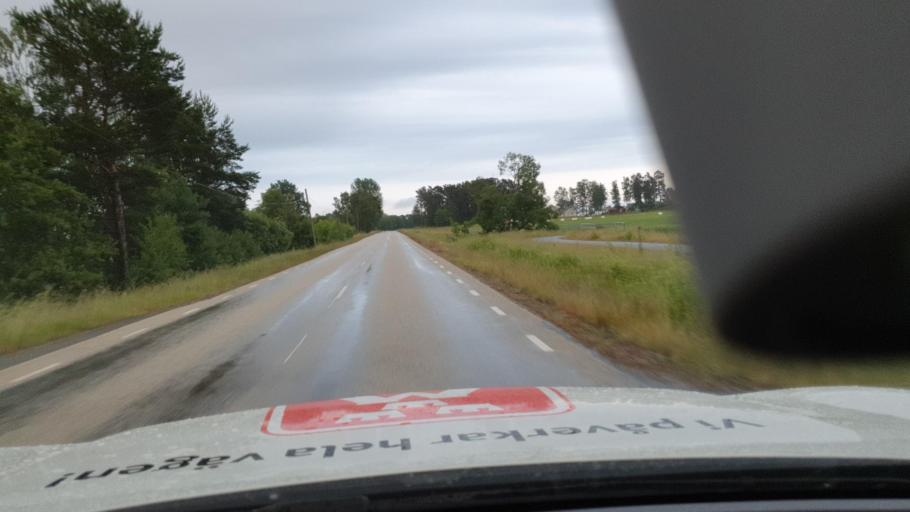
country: SE
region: Vaestra Goetaland
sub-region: Skovde Kommun
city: Stopen
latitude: 58.4793
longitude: 13.8792
